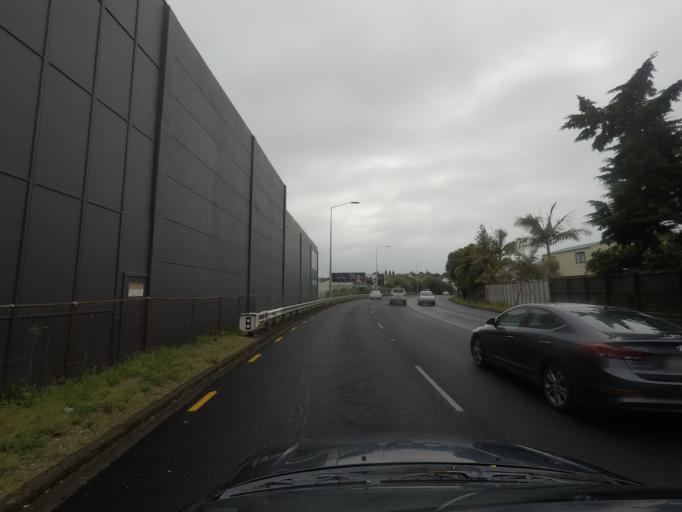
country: NZ
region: Auckland
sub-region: Auckland
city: Tamaki
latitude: -36.9013
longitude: 174.8130
